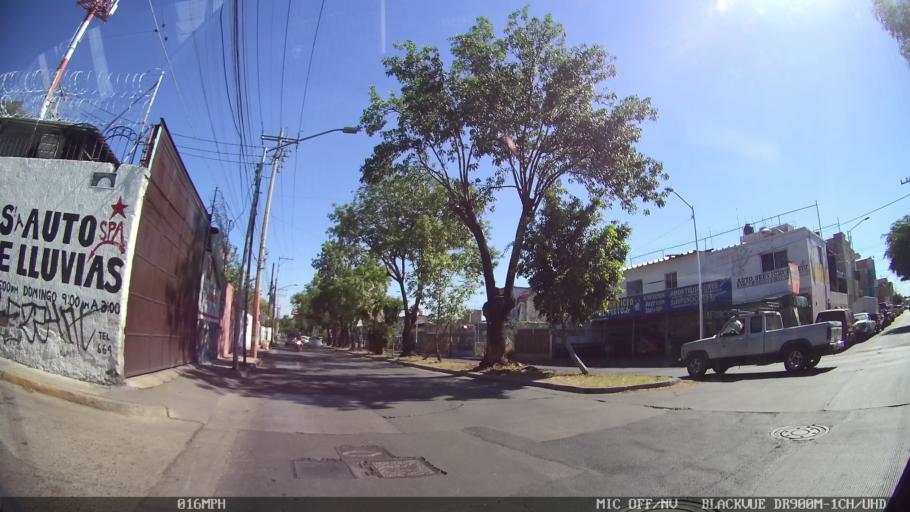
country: MX
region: Jalisco
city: Tlaquepaque
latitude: 20.6611
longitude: -103.2980
